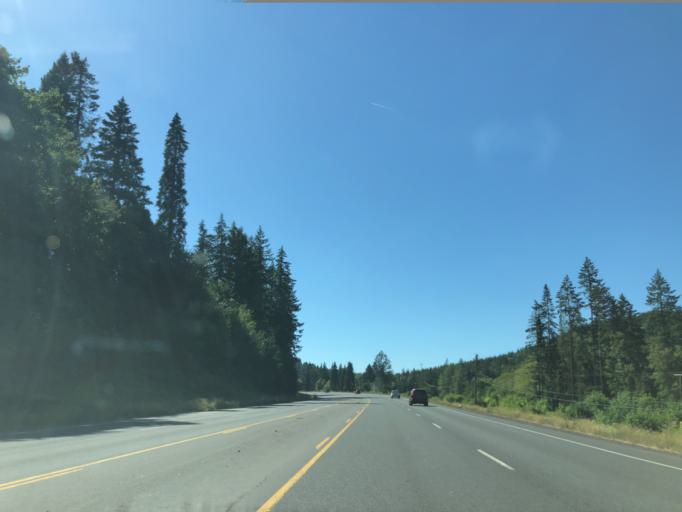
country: US
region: Oregon
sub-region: Linn County
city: Sweet Home
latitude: 44.4035
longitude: -122.7485
